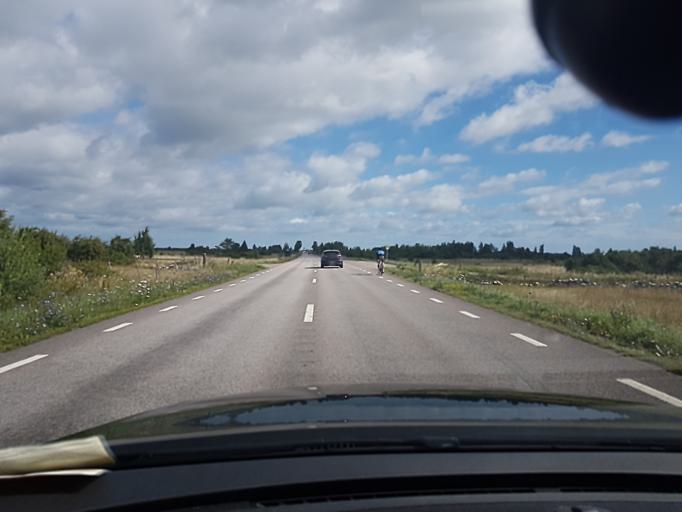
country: SE
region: Kalmar
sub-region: Borgholms Kommun
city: Borgholm
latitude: 56.9268
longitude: 16.7641
